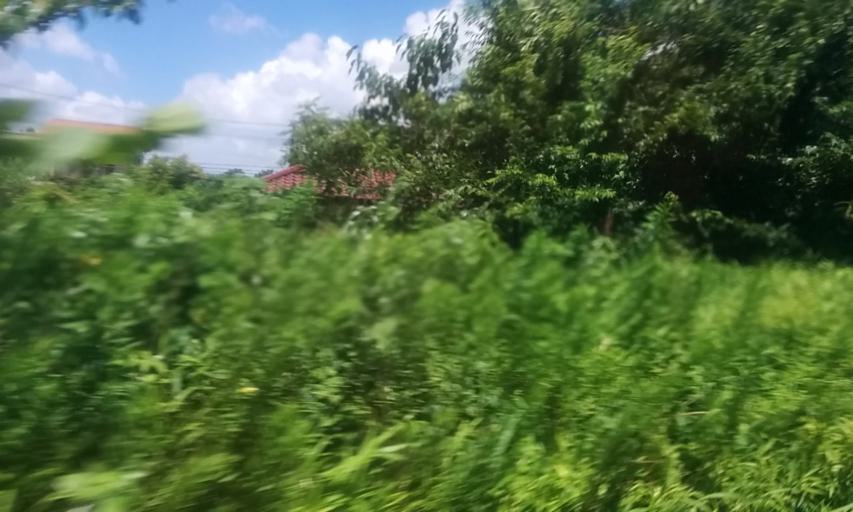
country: JP
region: Chiba
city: Oami
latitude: 35.5408
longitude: 140.2354
